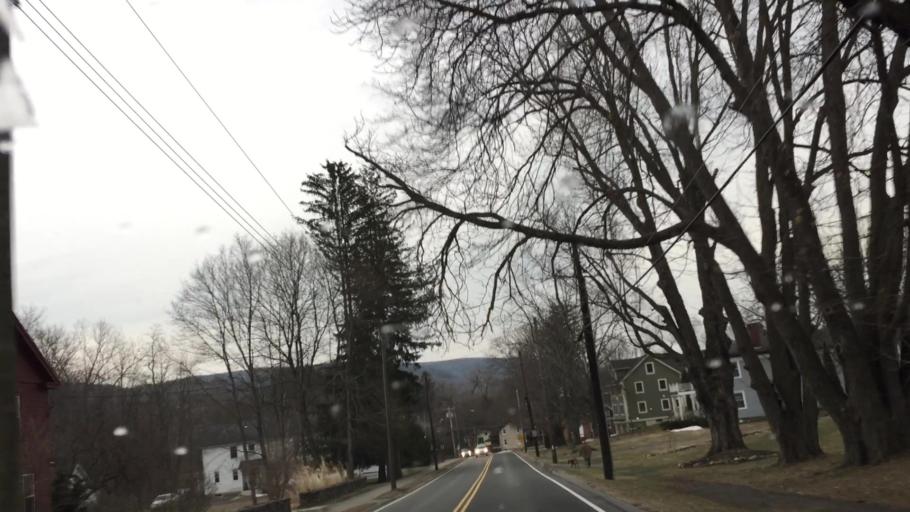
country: US
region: Massachusetts
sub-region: Berkshire County
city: Lee
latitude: 42.3343
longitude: -73.2489
